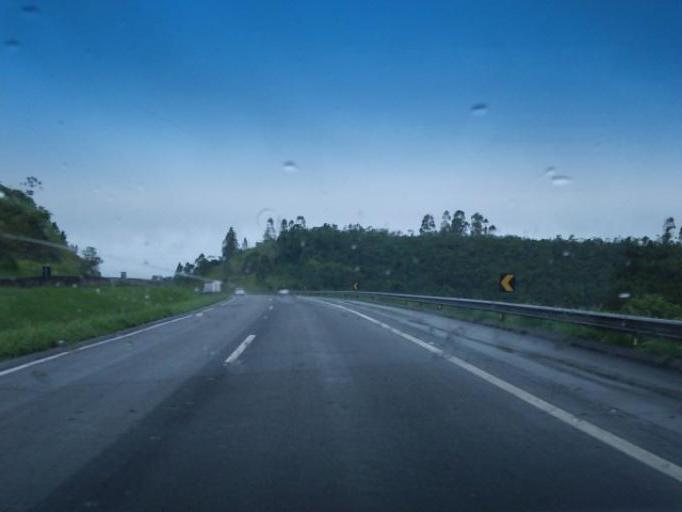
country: BR
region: Sao Paulo
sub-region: Cajati
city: Cajati
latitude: -24.7654
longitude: -48.1669
